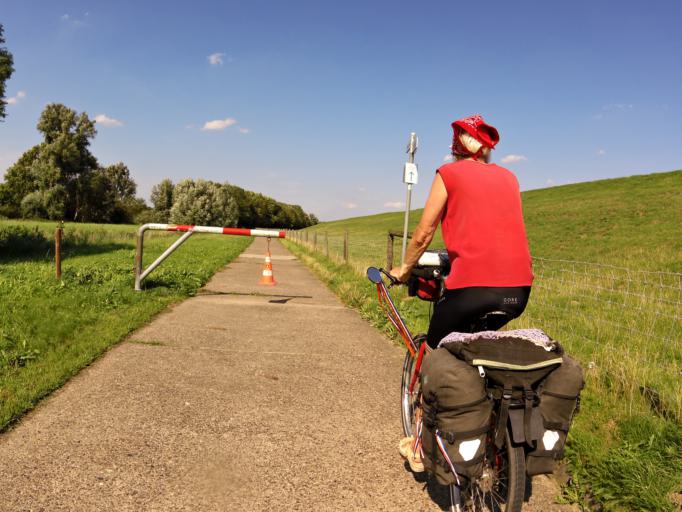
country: DE
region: Lower Saxony
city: Brake (Unterweser)
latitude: 53.4000
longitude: 8.4631
